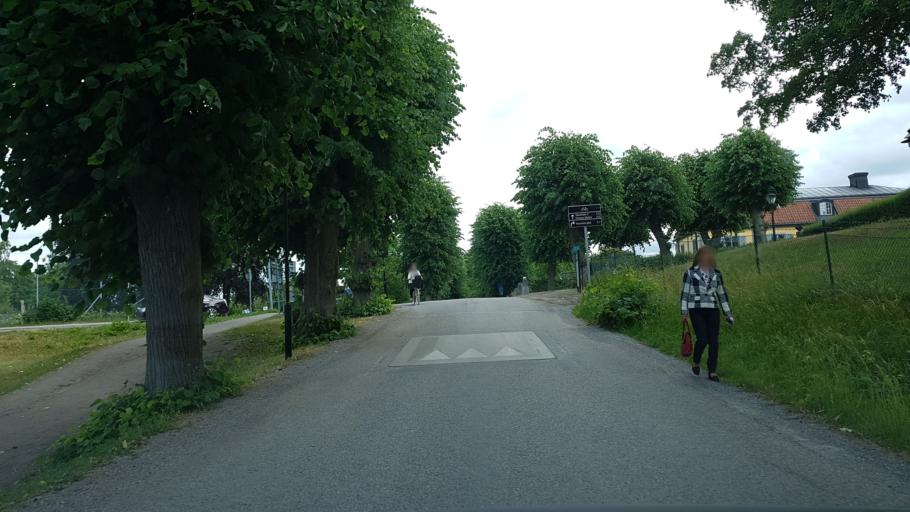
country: SE
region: Stockholm
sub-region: Solna Kommun
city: Solna
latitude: 59.3456
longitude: 17.9938
